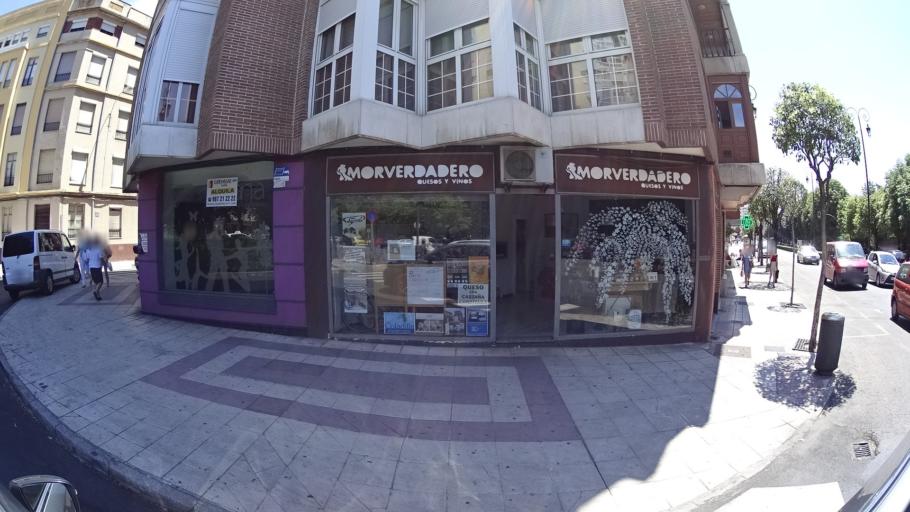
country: ES
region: Castille and Leon
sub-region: Provincia de Leon
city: Leon
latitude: 42.5997
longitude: -5.5806
